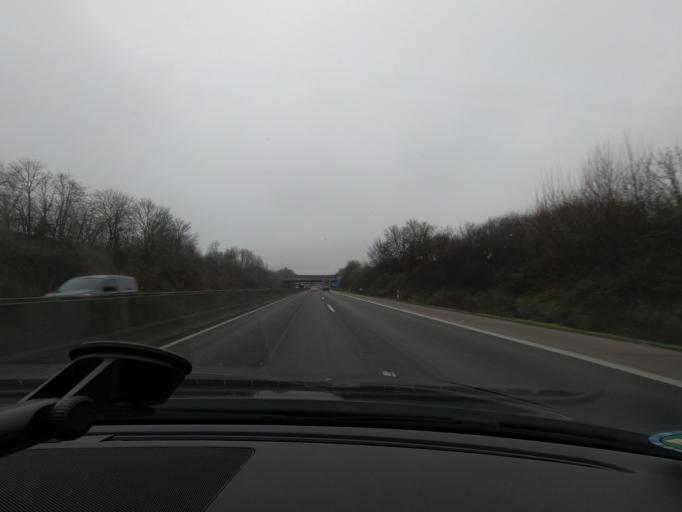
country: DE
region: North Rhine-Westphalia
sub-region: Regierungsbezirk Koln
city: Kerpen
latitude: 50.9044
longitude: 6.6893
